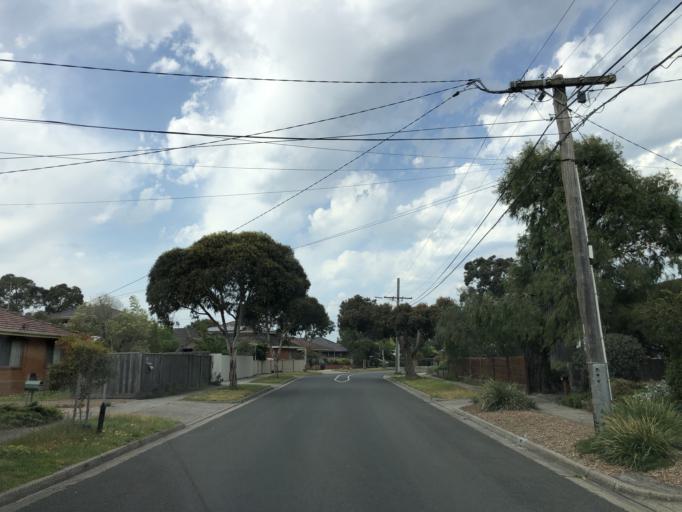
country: AU
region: Victoria
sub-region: Kingston
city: Carrum
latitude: -38.0851
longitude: 145.1310
